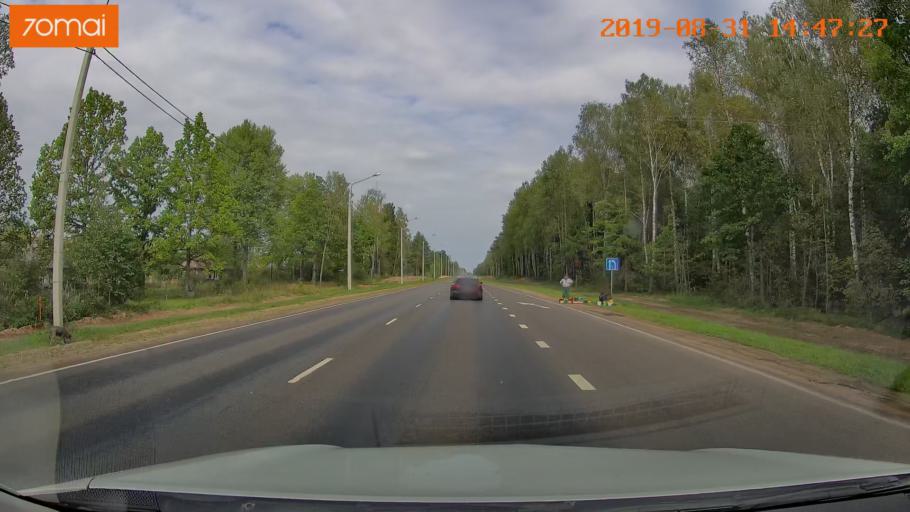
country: RU
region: Kaluga
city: Betlitsa
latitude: 54.2394
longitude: 33.7257
